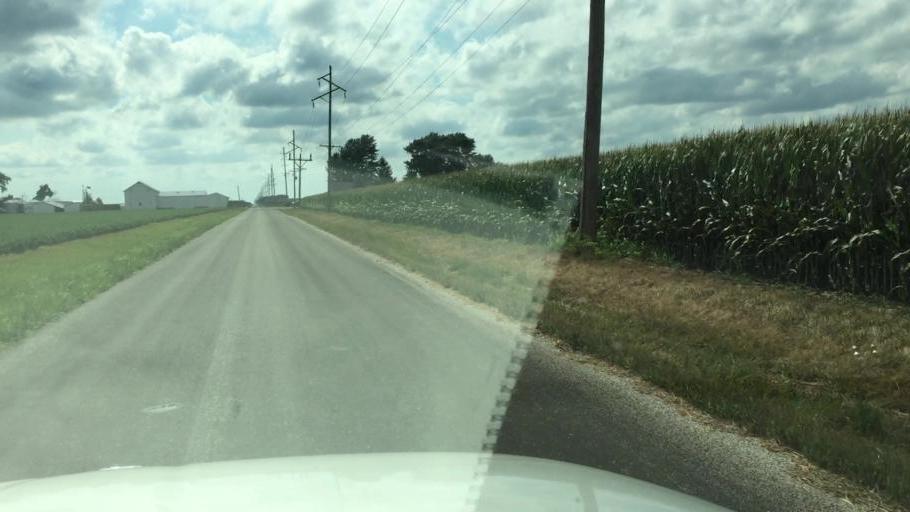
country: US
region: Illinois
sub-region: Hancock County
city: Carthage
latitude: 40.4169
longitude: -91.1752
